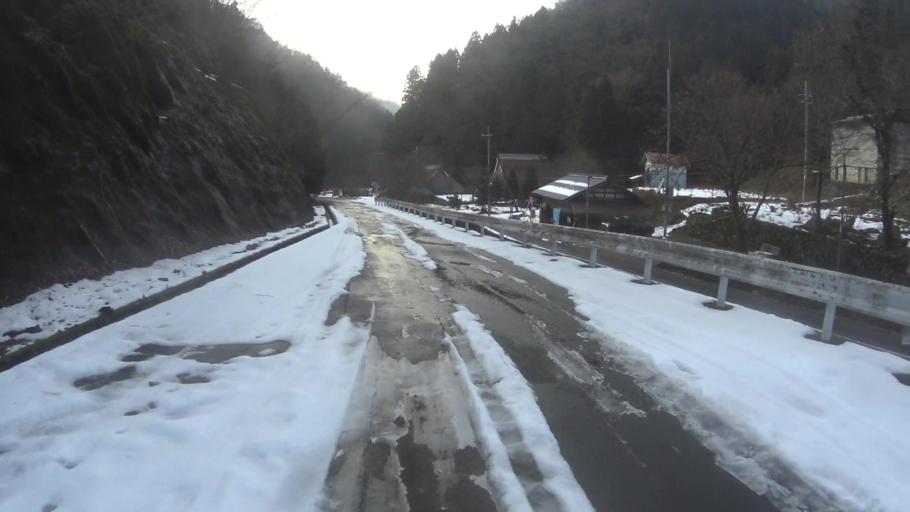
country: JP
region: Kyoto
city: Maizuru
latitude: 35.3547
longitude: 135.4820
